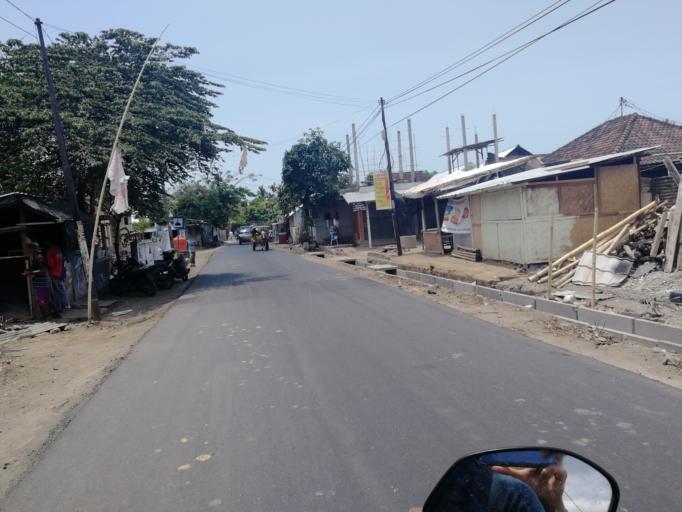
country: ID
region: West Nusa Tenggara
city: Pemenang
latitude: -8.4022
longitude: 116.1020
